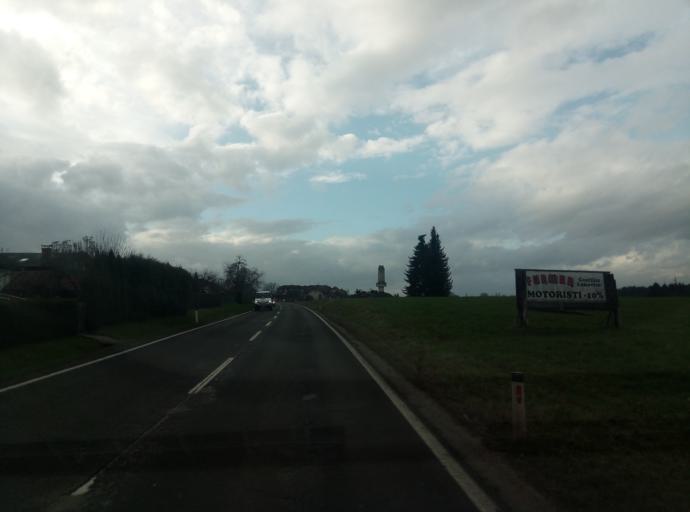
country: SI
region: Lukovica
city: Lukovica pri Domzalah
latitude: 46.1621
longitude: 14.6680
